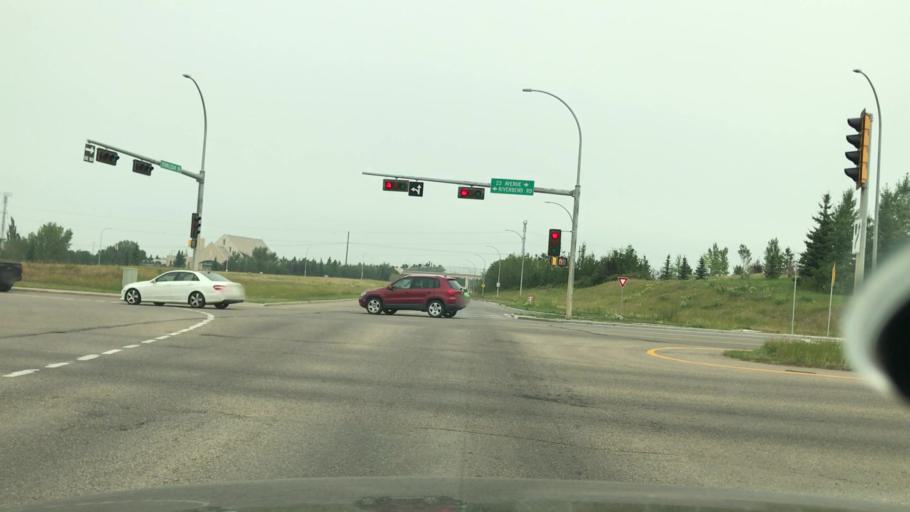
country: CA
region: Alberta
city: Edmonton
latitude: 53.4572
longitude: -113.5883
